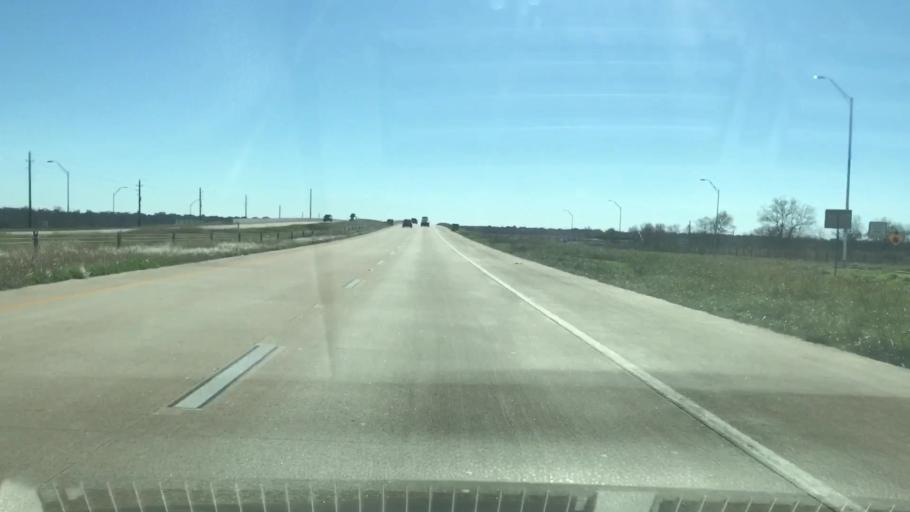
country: US
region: Texas
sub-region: Harris County
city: Cypress
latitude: 29.9813
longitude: -95.7697
